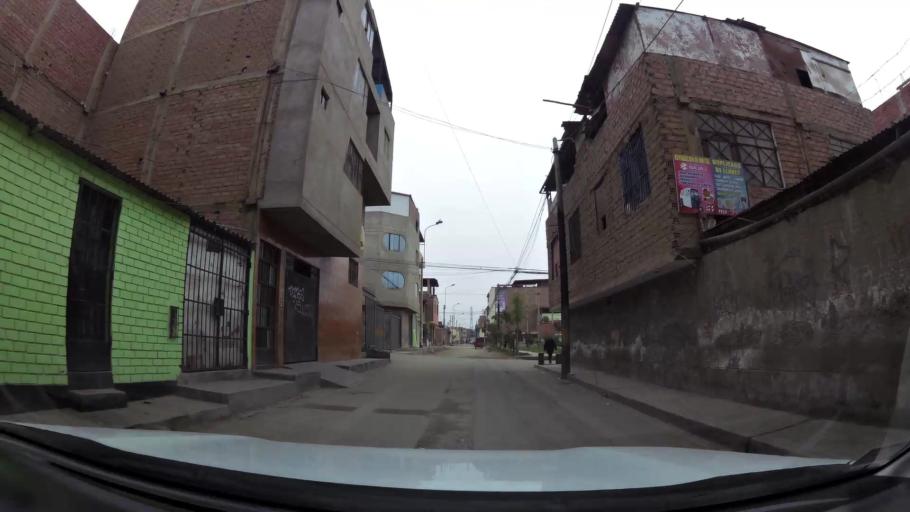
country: PE
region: Lima
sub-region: Lima
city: Surco
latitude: -12.1753
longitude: -76.9638
